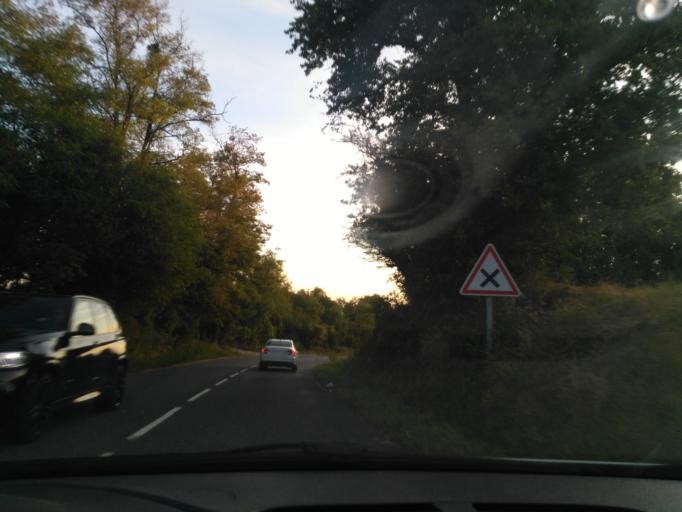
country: FR
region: Rhone-Alpes
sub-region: Departement du Rhone
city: Limonest
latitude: 45.8444
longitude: 4.7937
